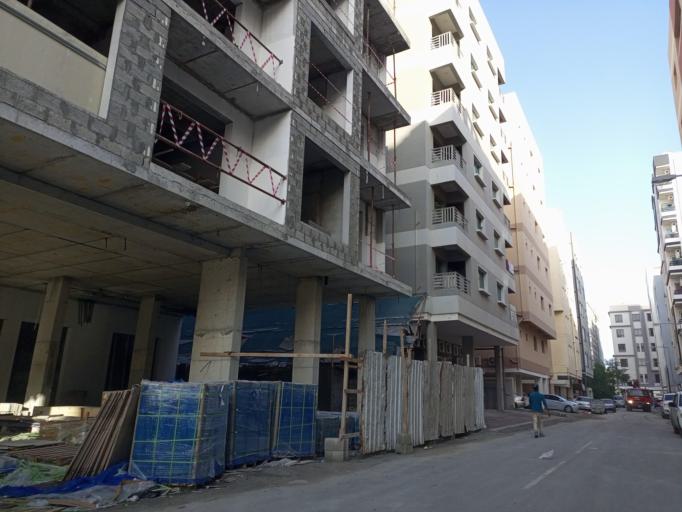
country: BH
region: Muharraq
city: Al Hadd
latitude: 26.2331
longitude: 50.6457
